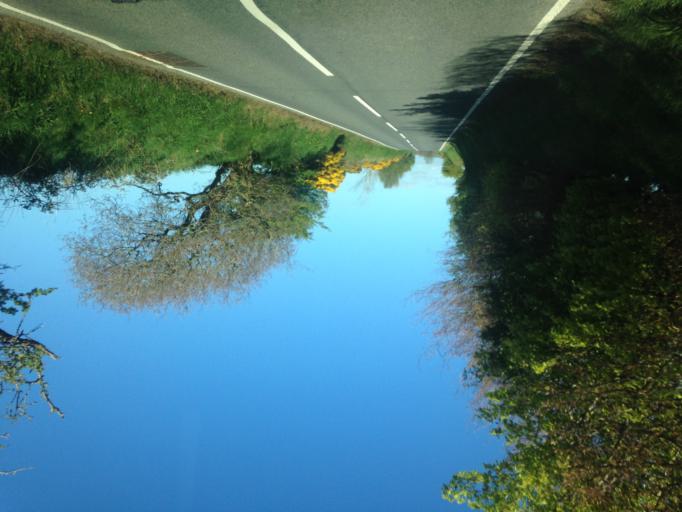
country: GB
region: Wales
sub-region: County of Ceredigion
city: Llanllwchaiarn
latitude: 52.0958
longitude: -4.3876
